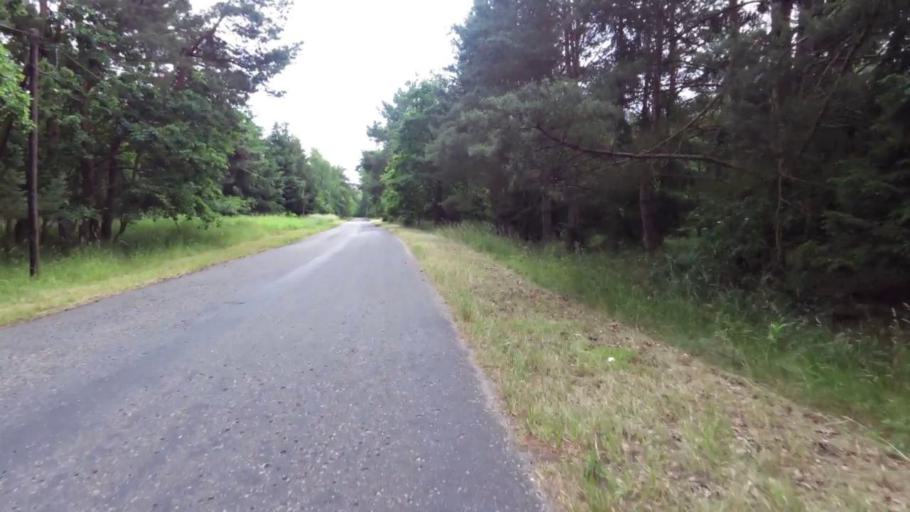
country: PL
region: West Pomeranian Voivodeship
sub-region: Powiat goleniowski
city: Stepnica
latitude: 53.7085
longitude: 14.5514
